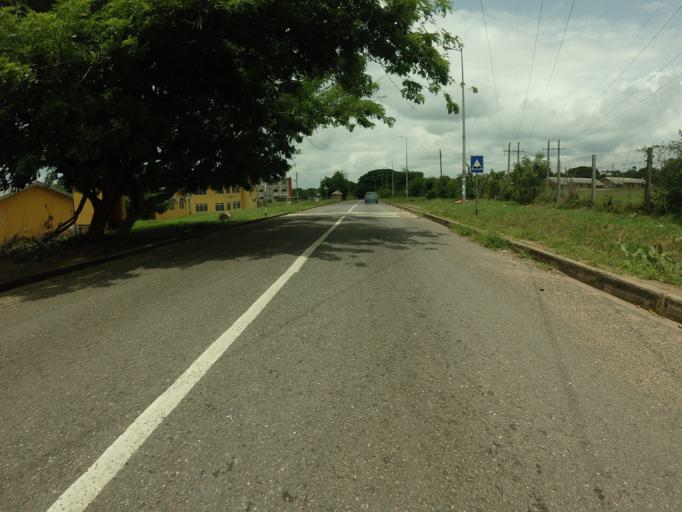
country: GH
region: Volta
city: Ho
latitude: 6.6000
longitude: 0.4798
